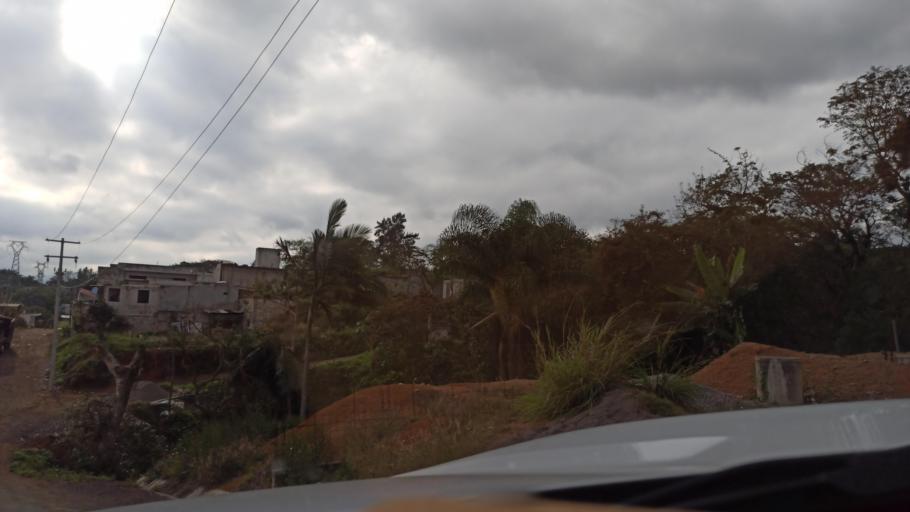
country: MX
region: Veracruz
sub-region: Fortin
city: Fraccionamiento Villas de la Llave
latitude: 18.9162
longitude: -96.9988
